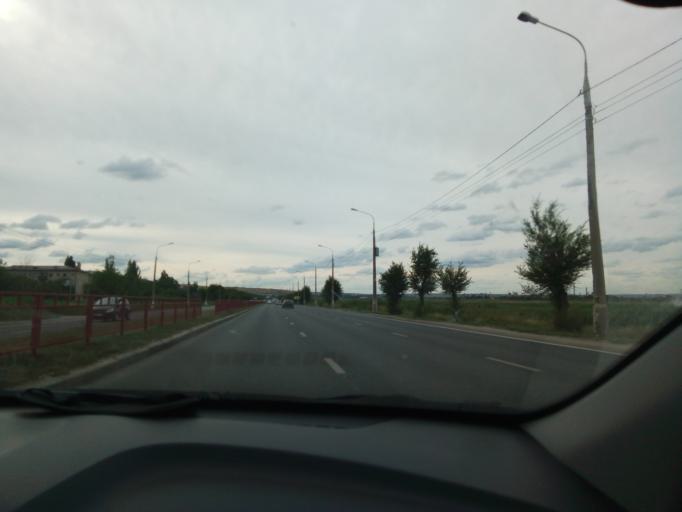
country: RU
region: Volgograd
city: Volgograd
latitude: 48.5263
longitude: 44.4864
